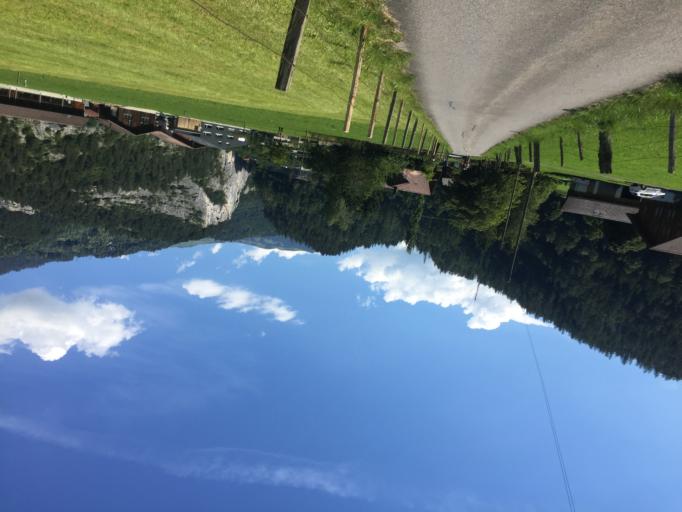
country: CH
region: Bern
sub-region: Interlaken-Oberhasli District
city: Meiringen
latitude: 46.7057
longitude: 8.2185
